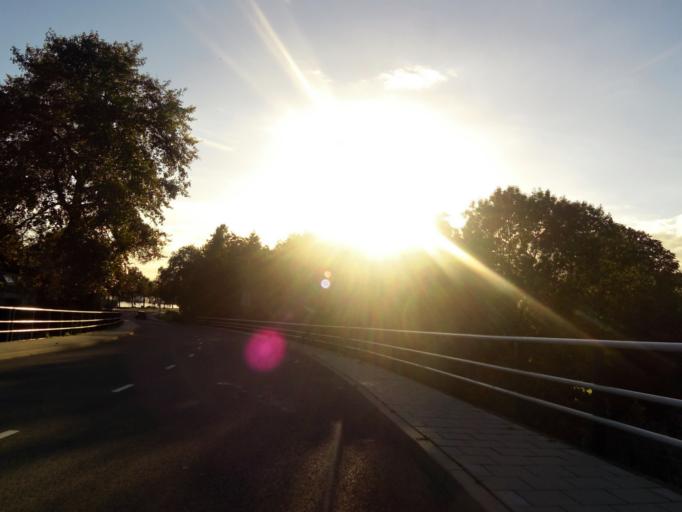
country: NL
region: South Holland
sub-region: Gemeente Alphen aan den Rijn
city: Alphen aan den Rijn
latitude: 52.1429
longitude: 4.6460
